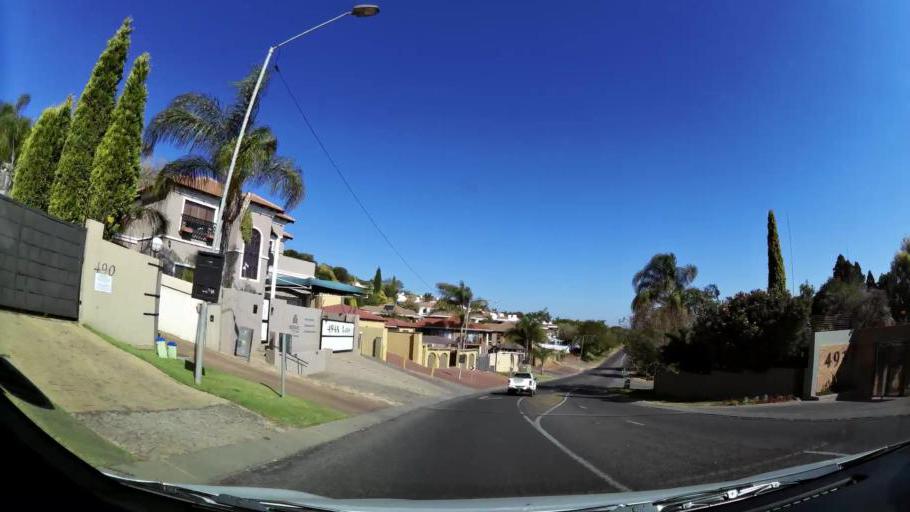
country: ZA
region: Gauteng
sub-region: City of Tshwane Metropolitan Municipality
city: Centurion
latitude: -25.8098
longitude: 28.2705
